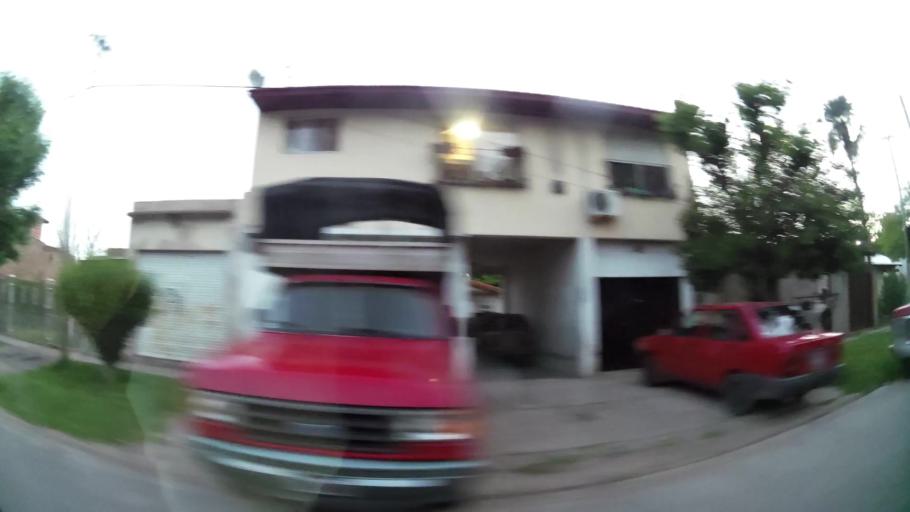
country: AR
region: Buenos Aires
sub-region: Partido de Quilmes
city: Quilmes
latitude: -34.8021
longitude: -58.2849
